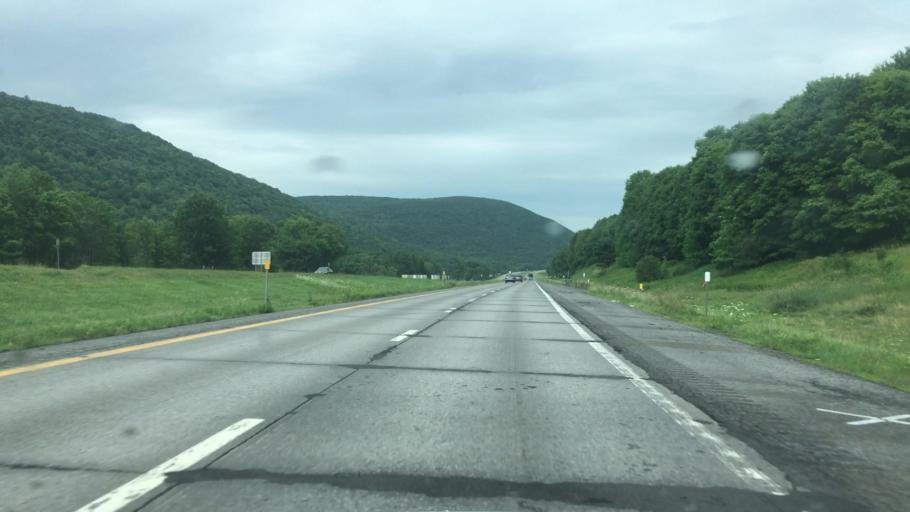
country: US
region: New York
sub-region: Otsego County
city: Worcester
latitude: 42.6321
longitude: -74.6583
